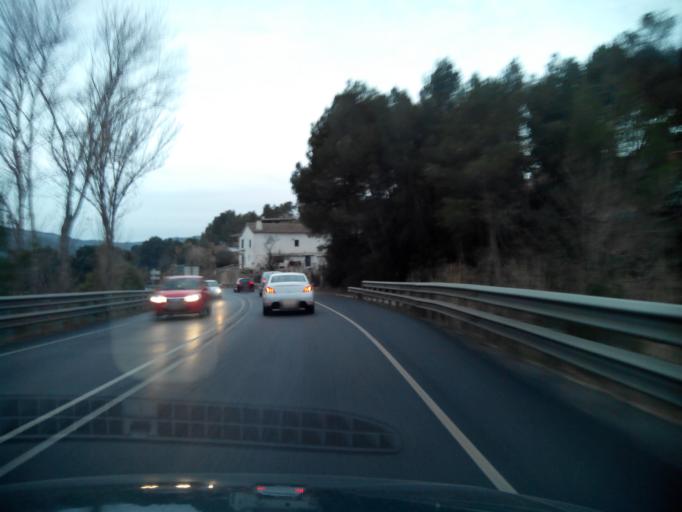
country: ES
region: Catalonia
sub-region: Provincia de Barcelona
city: Monistrol de Montserrat
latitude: 41.6129
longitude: 1.8731
